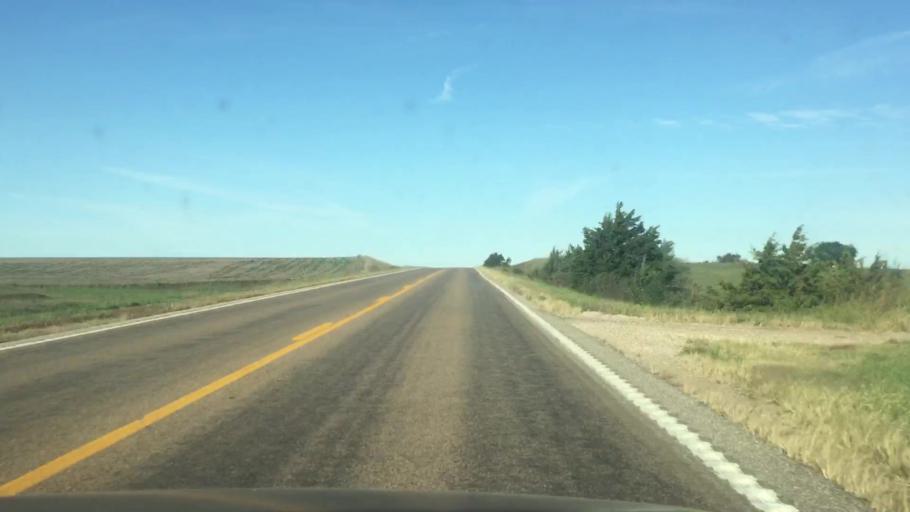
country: US
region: Nebraska
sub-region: Thayer County
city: Hebron
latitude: 40.1474
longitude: -97.5268
